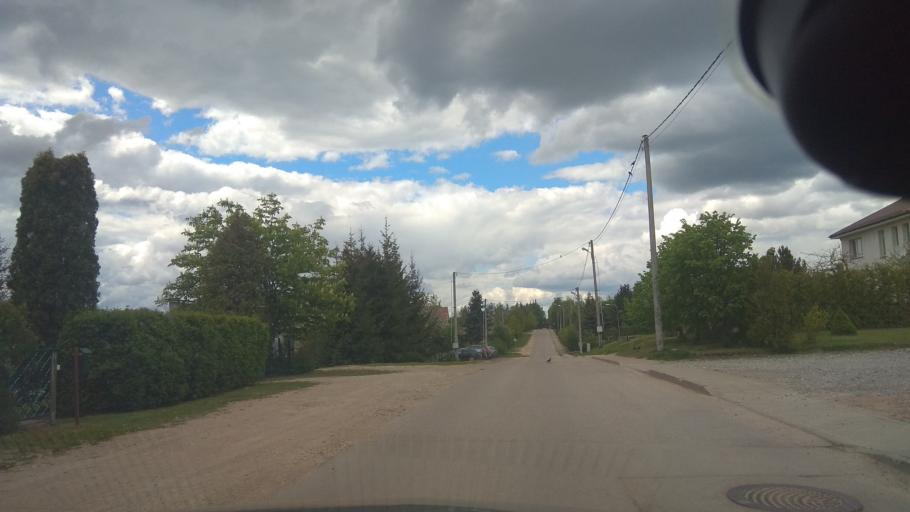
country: LT
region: Vilnius County
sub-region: Vilnius
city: Fabijoniskes
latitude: 54.8041
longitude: 25.2650
